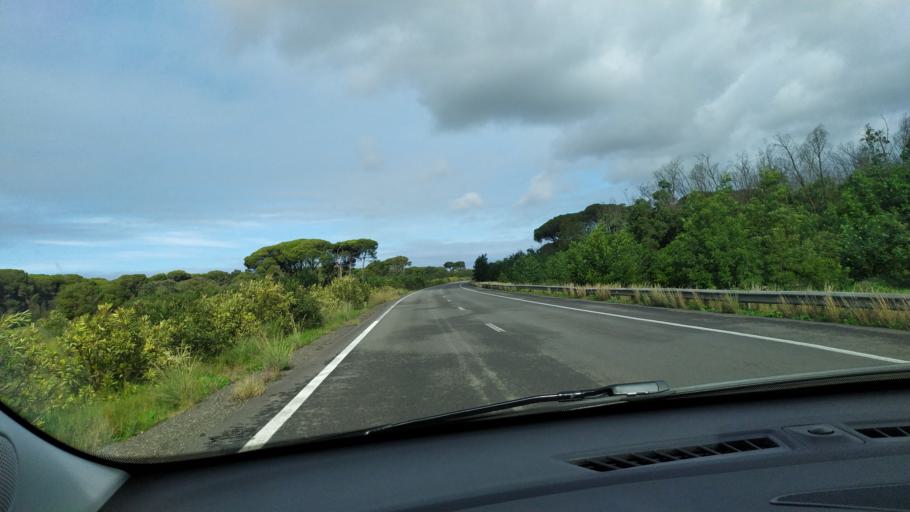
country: MA
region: Tanger-Tetouan
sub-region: Larache
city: Larache
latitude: 35.1300
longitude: -6.1464
